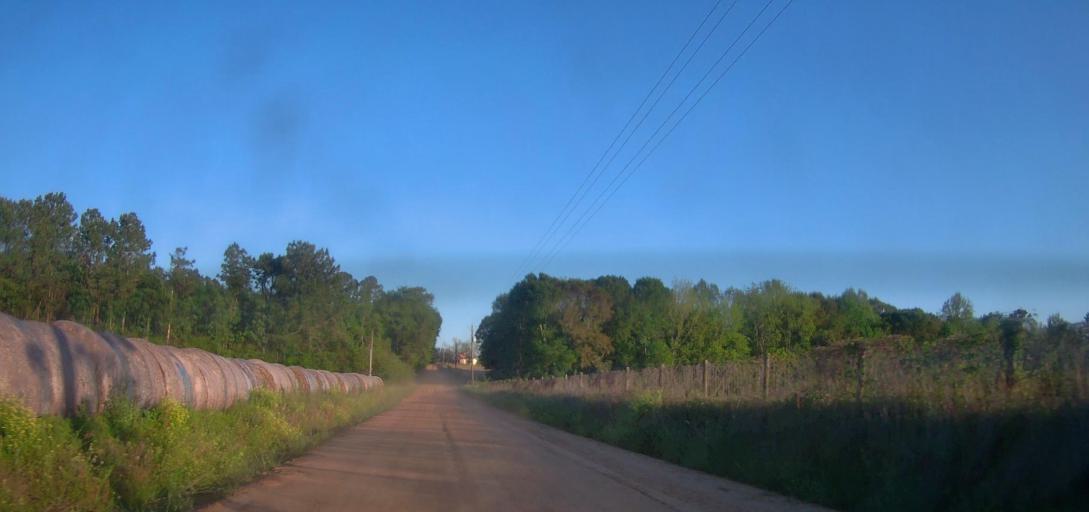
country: US
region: Georgia
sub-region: Irwin County
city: Ocilla
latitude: 31.6462
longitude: -83.2237
